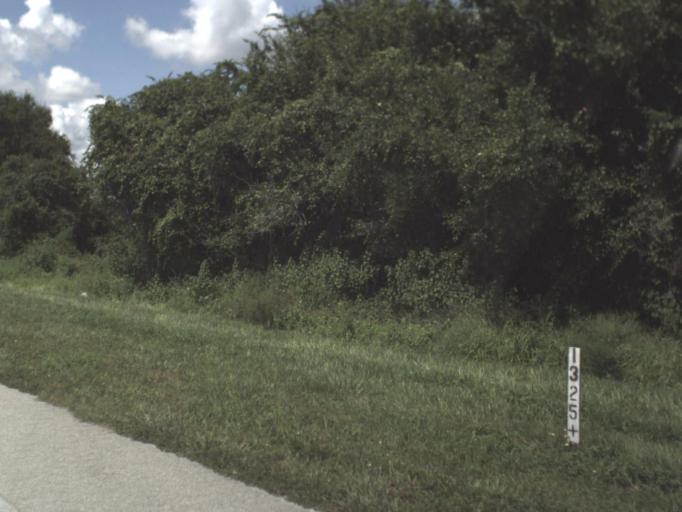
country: US
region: Florida
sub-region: DeSoto County
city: Nocatee
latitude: 27.1134
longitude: -81.9237
